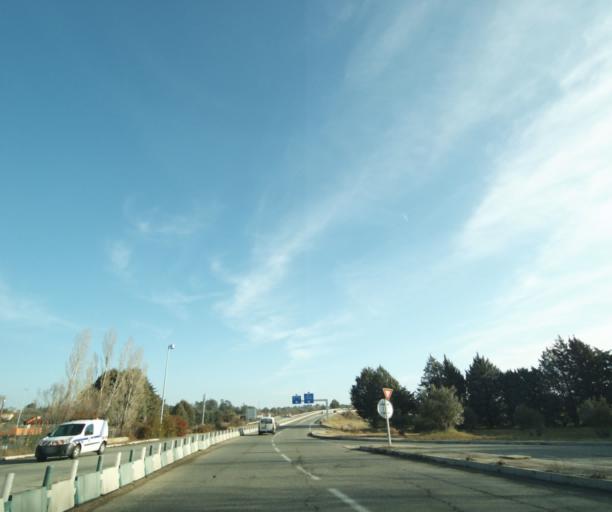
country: FR
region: Provence-Alpes-Cote d'Azur
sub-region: Departement du Var
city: Saint-Maximin-la-Sainte-Baume
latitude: 43.4497
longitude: 5.8777
